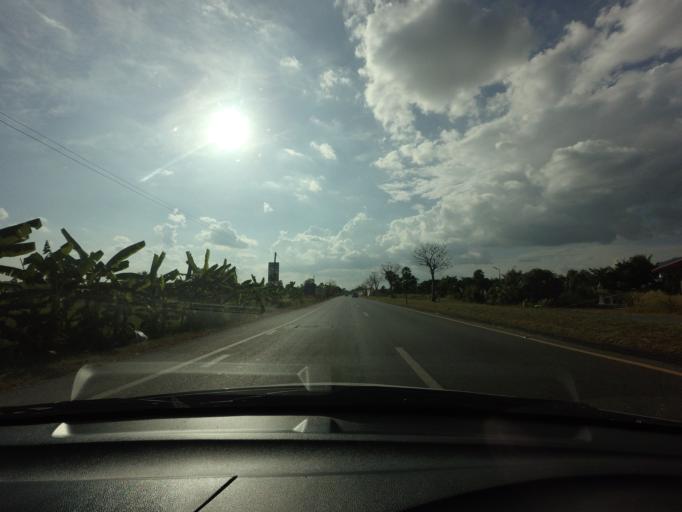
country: TH
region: Nakhon Nayok
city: Nakhon Nayok
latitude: 14.2216
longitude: 101.2188
